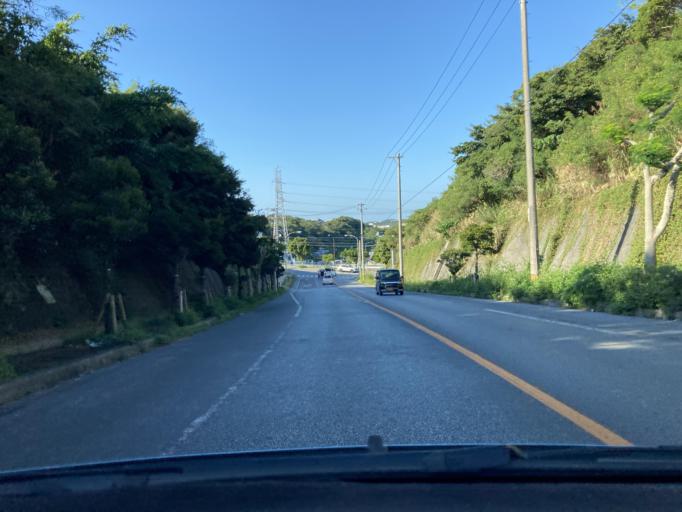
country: JP
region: Okinawa
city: Chatan
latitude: 26.2881
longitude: 127.7857
